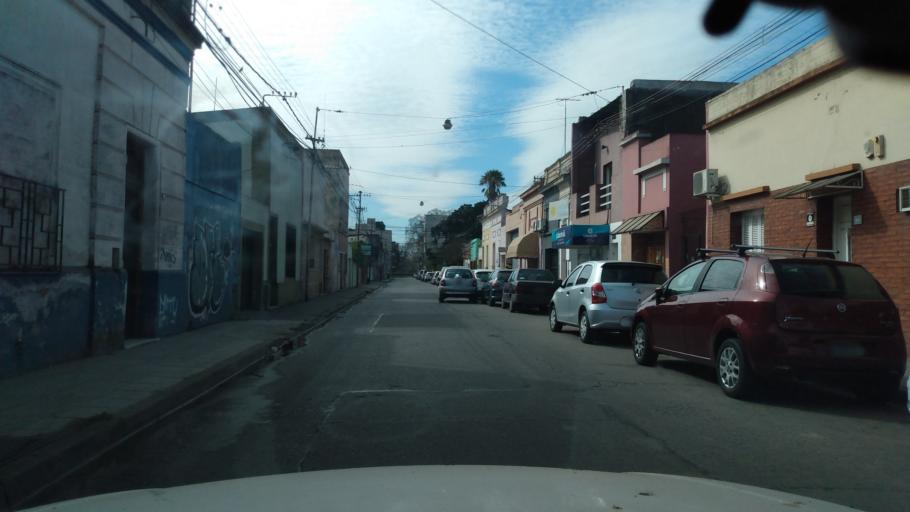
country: AR
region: Buenos Aires
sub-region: Partido de Lujan
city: Lujan
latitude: -34.5622
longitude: -59.1168
